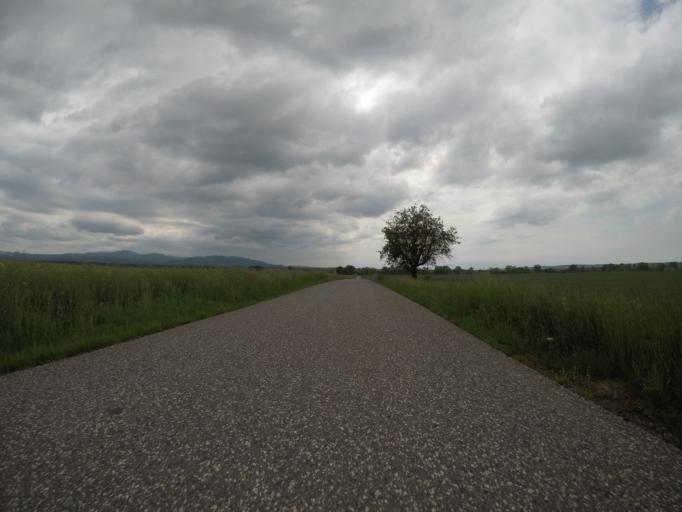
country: SK
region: Nitriansky
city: Sahy
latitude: 48.0689
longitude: 18.8590
